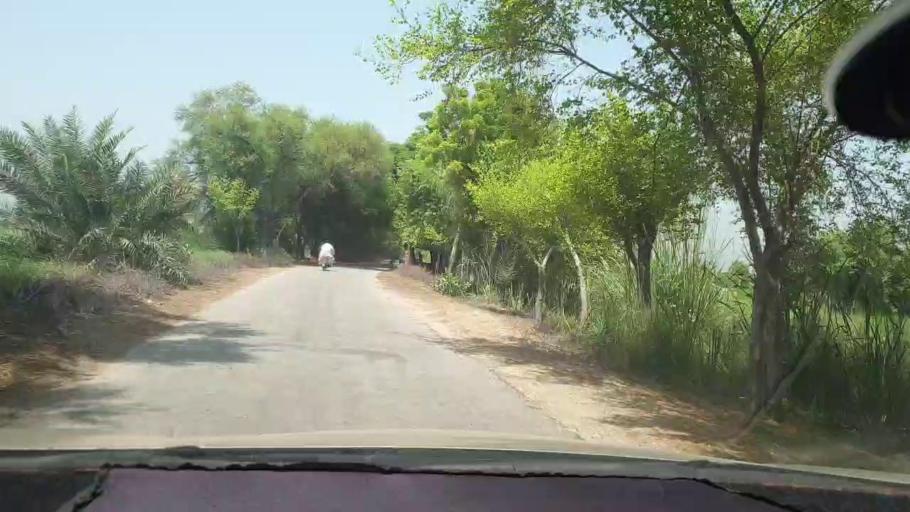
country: PK
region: Sindh
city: Kambar
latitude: 27.6410
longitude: 67.9743
